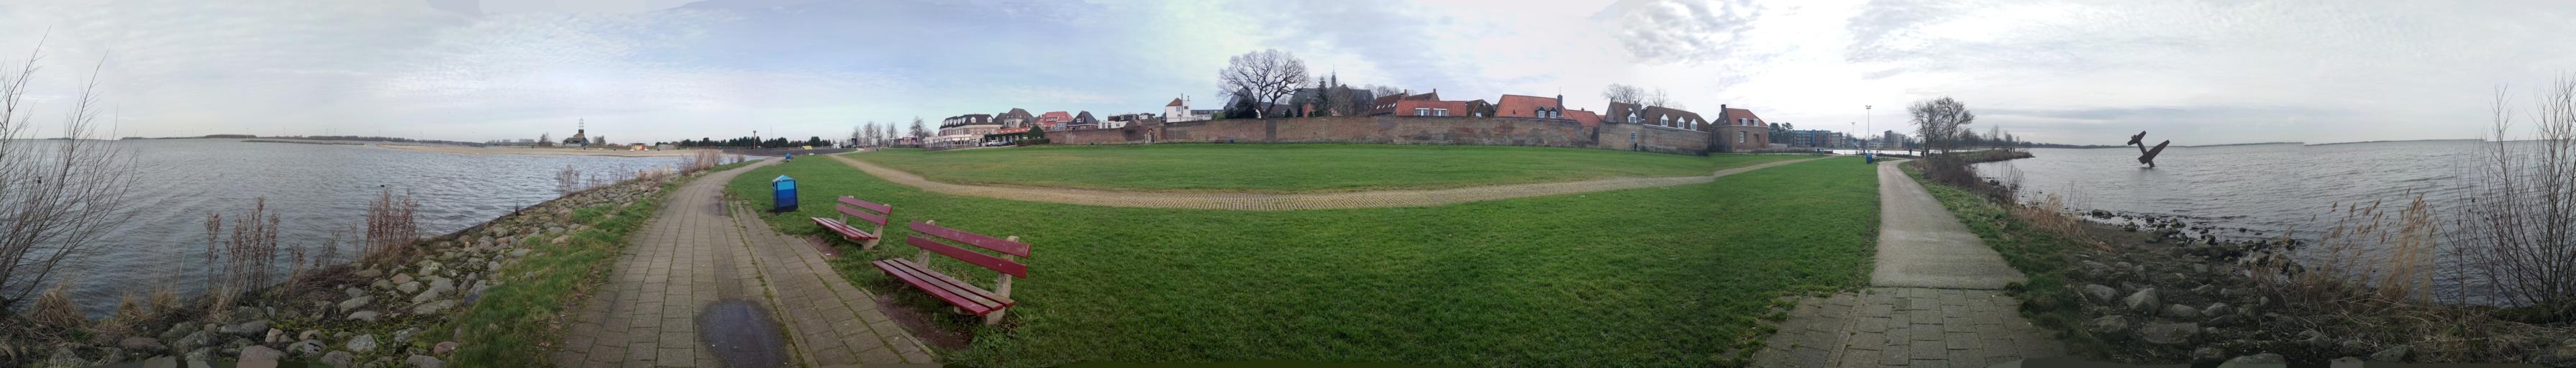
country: NL
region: Gelderland
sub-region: Gemeente Harderwijk
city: Harderwijk
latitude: 52.3500
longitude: 5.6134
